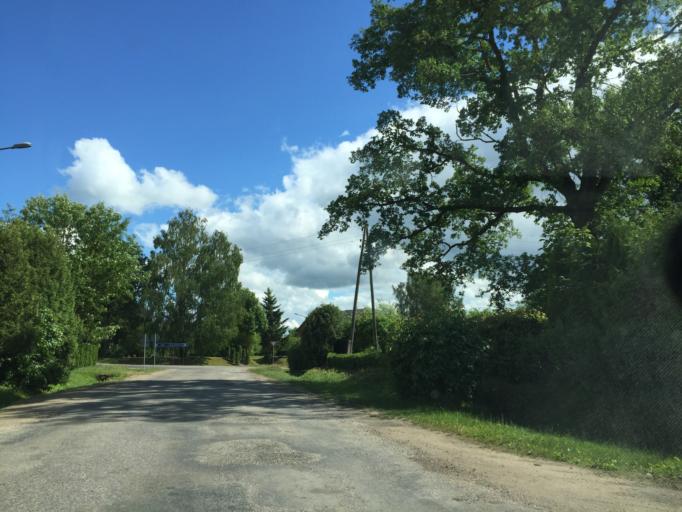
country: LT
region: Panevezys
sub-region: Birzai
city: Birzai
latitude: 56.3823
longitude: 24.6449
